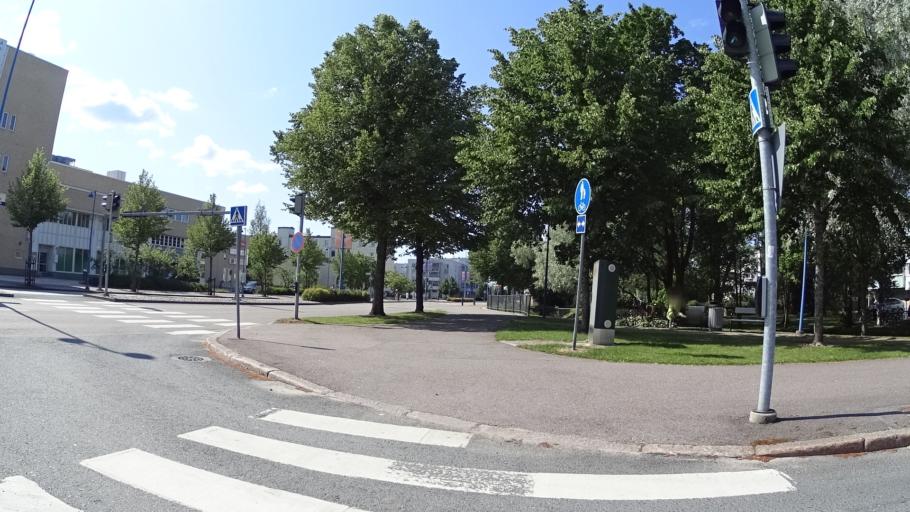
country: FI
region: Uusimaa
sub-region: Helsinki
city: Jaervenpaeae
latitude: 60.4739
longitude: 25.0851
